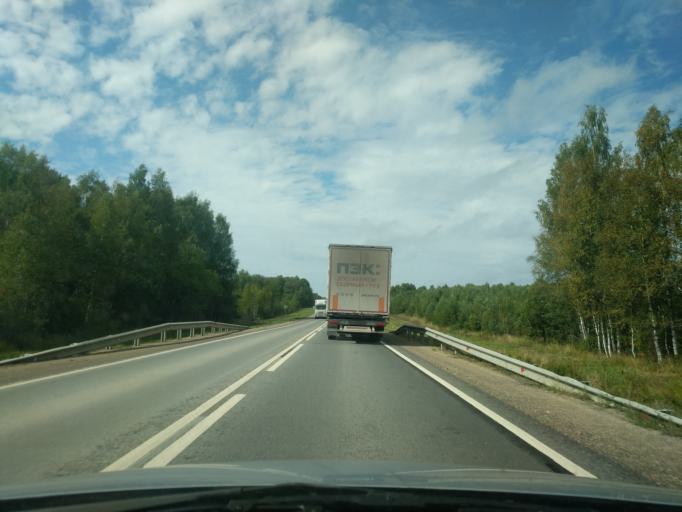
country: RU
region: Kostroma
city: Sudislavl'
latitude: 57.8616
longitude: 41.7707
